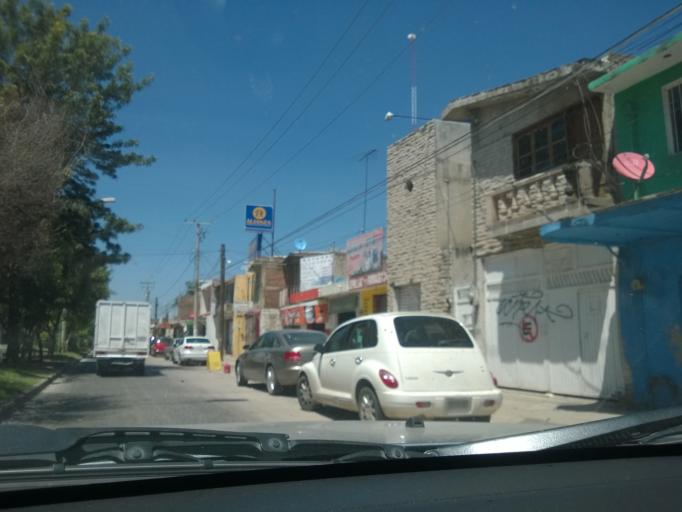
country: MX
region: Guanajuato
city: Leon
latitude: 21.1183
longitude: -101.6421
